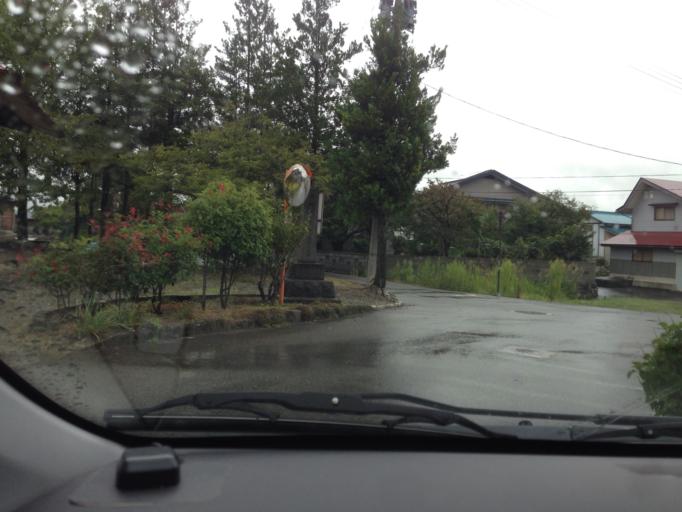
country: JP
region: Fukushima
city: Kitakata
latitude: 37.5146
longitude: 139.8265
